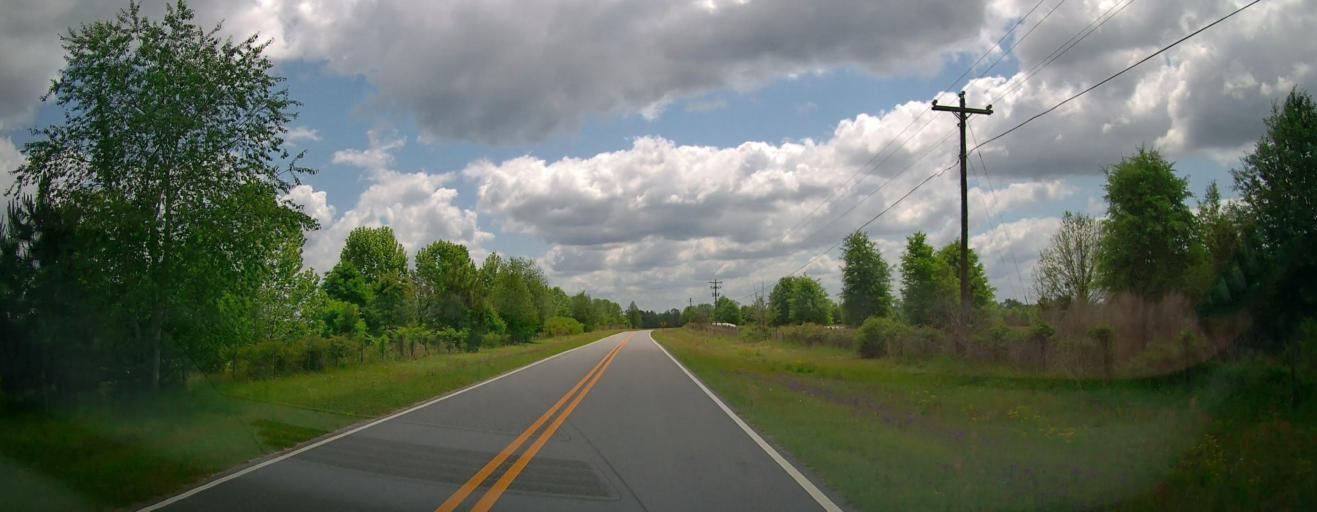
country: US
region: Georgia
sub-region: Laurens County
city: Dublin
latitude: 32.5983
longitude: -82.9327
